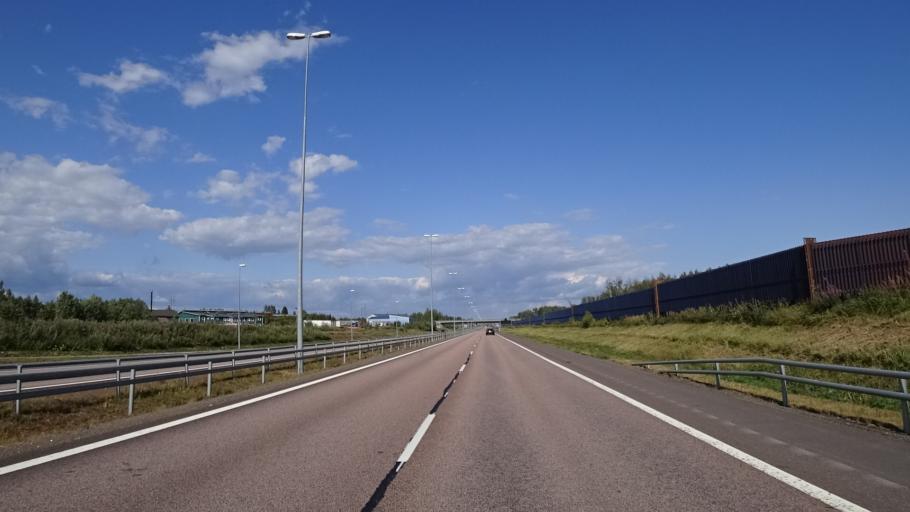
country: FI
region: Kymenlaakso
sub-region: Kotka-Hamina
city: Hamina
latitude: 60.5765
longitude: 27.1378
